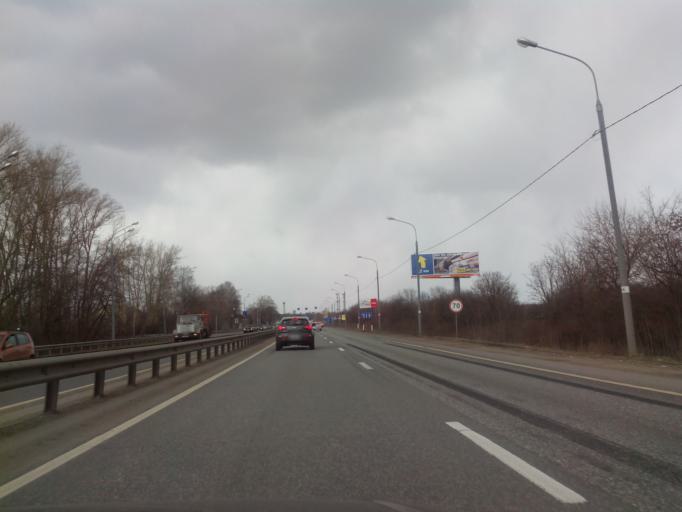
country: RU
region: Moskovskaya
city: Noginsk
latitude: 55.8335
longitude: 38.3929
